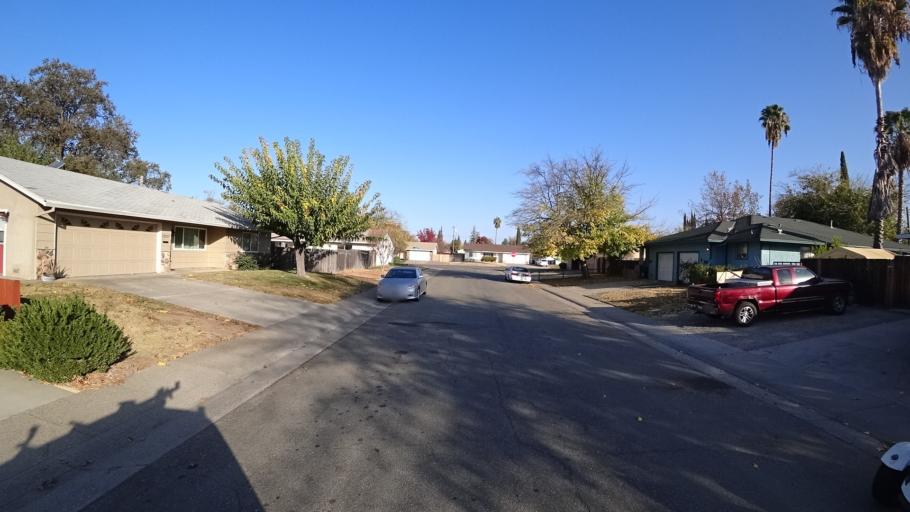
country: US
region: California
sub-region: Sacramento County
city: Citrus Heights
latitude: 38.6975
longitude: -121.2684
